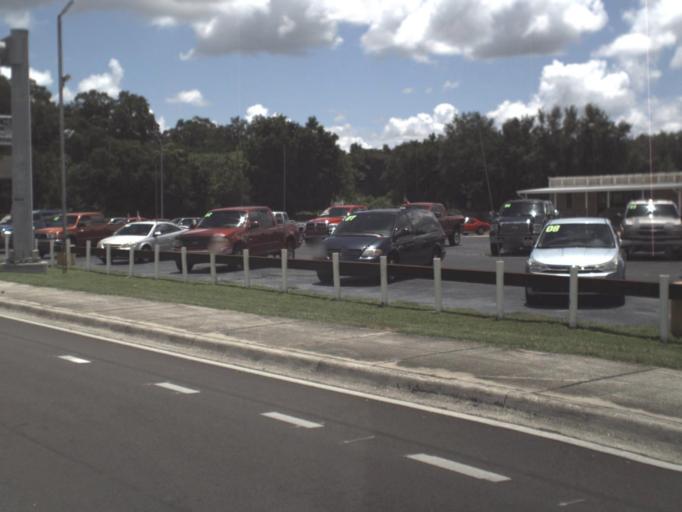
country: US
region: Florida
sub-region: Hillsborough County
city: Mango
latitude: 27.9815
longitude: -82.3001
